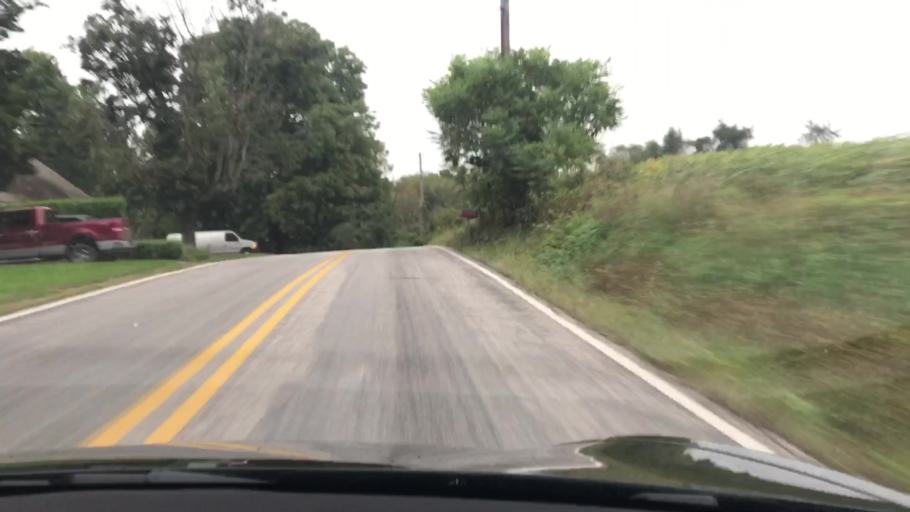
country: US
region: Pennsylvania
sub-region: York County
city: Weigelstown
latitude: 39.9440
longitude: -76.8617
